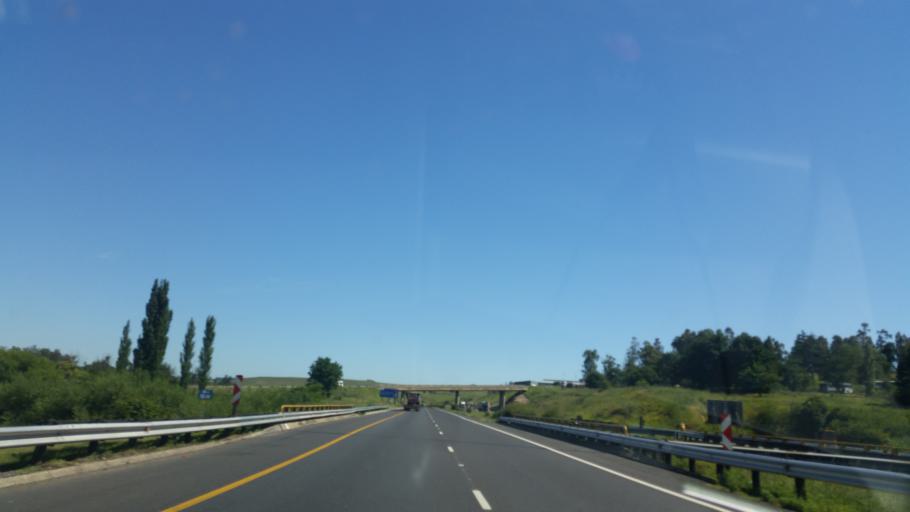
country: ZA
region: KwaZulu-Natal
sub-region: uMgungundlovu District Municipality
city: Mooirivier
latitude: -29.2077
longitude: 30.0018
